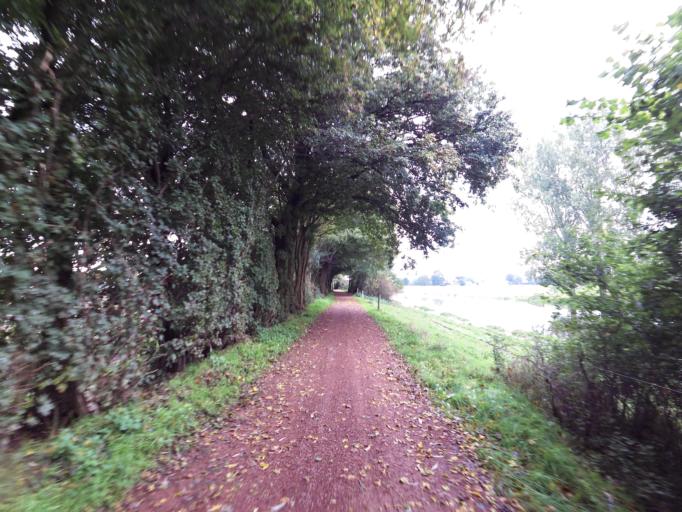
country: DE
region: North Rhine-Westphalia
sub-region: Regierungsbezirk Munster
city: Isselburg
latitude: 51.8488
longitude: 6.5251
